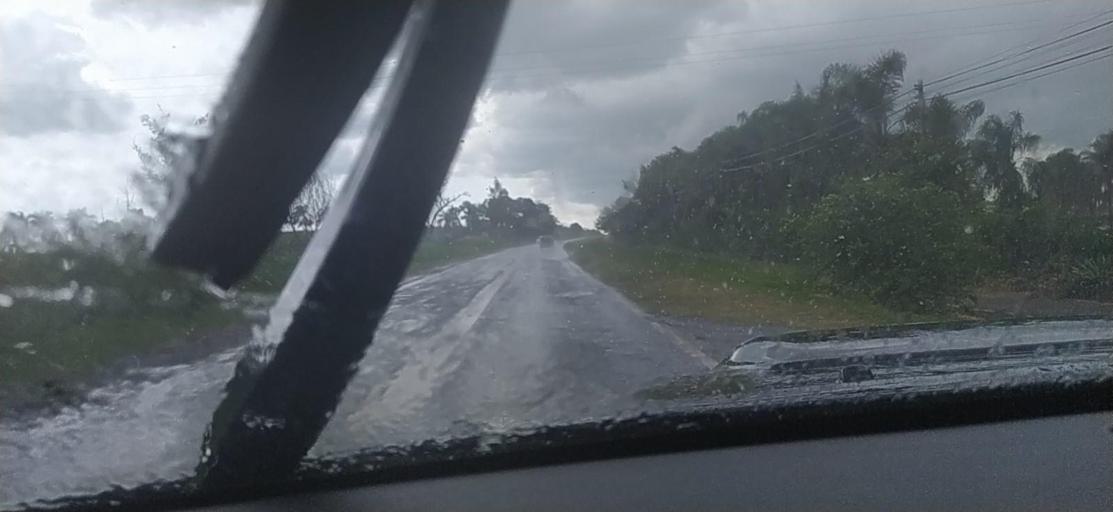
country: BR
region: Sao Paulo
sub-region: Catanduva
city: Catanduva
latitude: -21.1590
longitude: -48.9483
